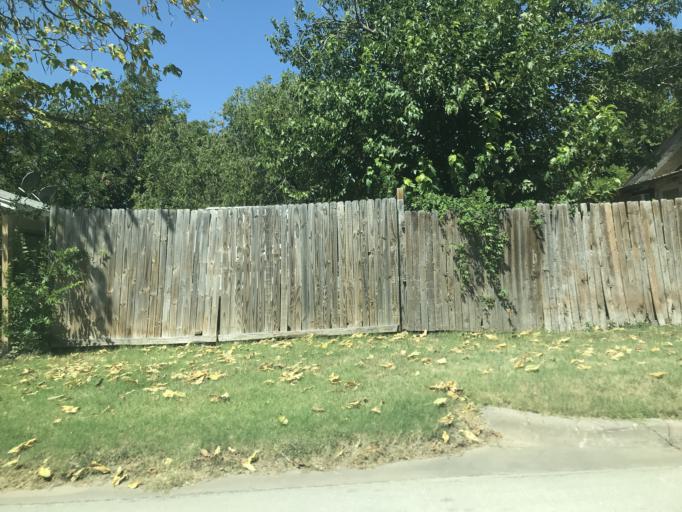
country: US
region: Texas
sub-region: Taylor County
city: Abilene
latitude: 32.4380
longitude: -99.7432
